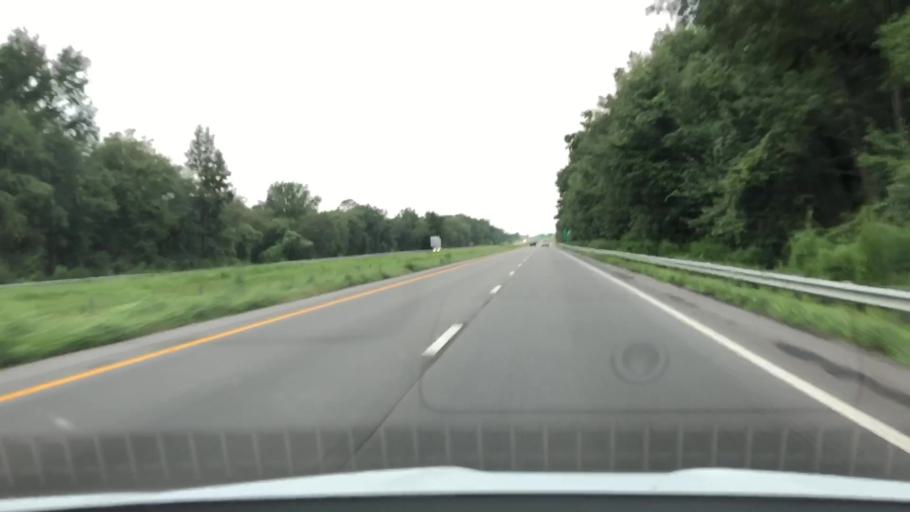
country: US
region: North Carolina
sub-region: Lenoir County
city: La Grange
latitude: 35.2945
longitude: -77.8034
